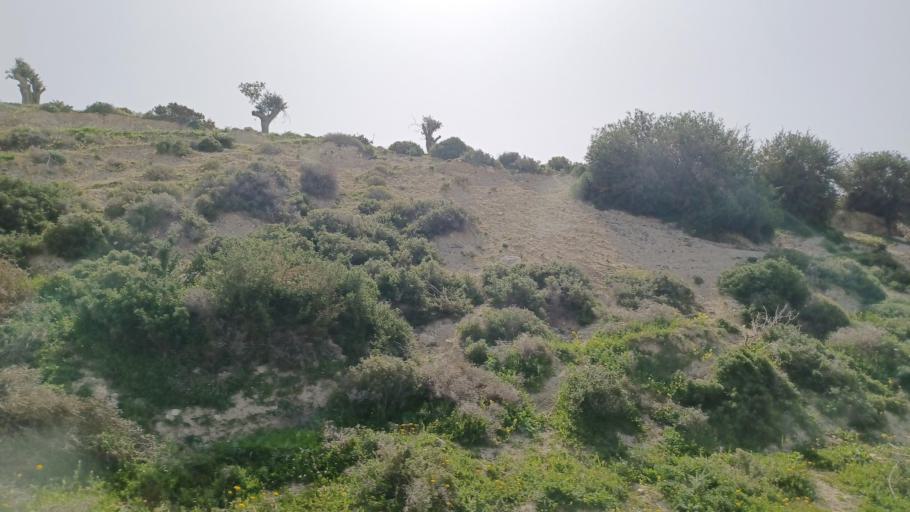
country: CY
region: Limassol
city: Pissouri
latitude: 34.6917
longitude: 32.7065
